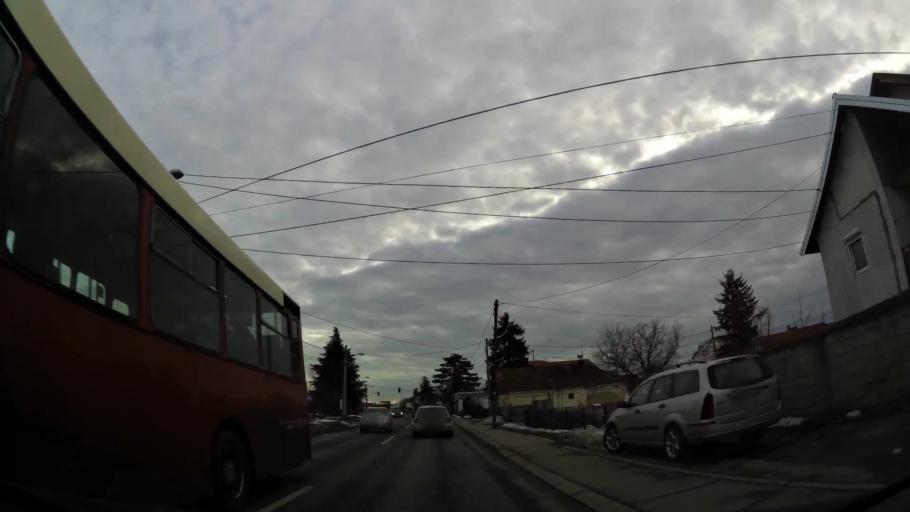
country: RS
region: Central Serbia
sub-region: Belgrade
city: Rakovica
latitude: 44.7327
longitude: 20.4830
